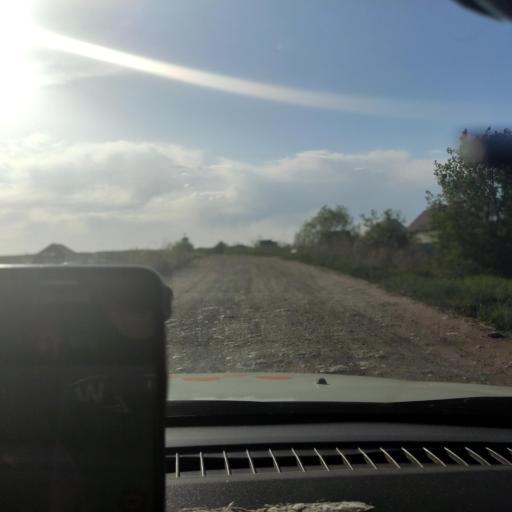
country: RU
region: Bashkortostan
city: Avdon
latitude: 54.5118
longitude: 55.8155
